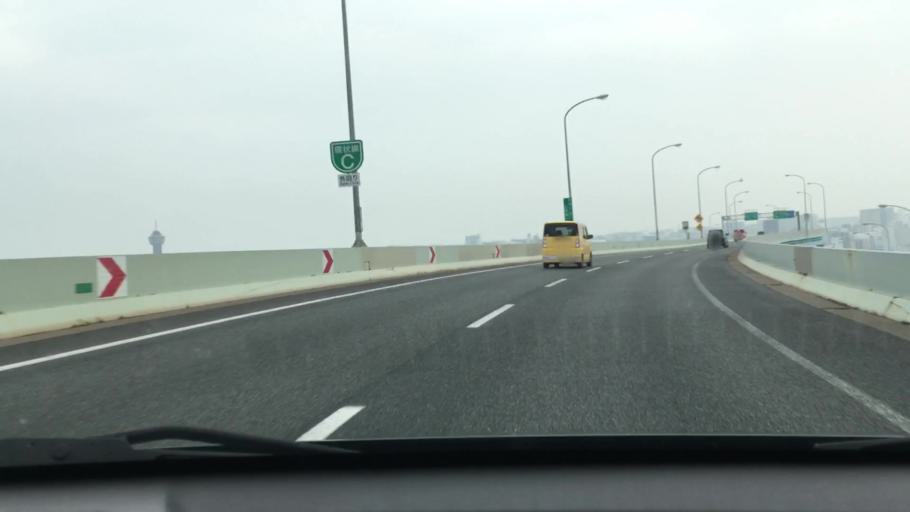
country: JP
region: Fukuoka
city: Fukuoka-shi
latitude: 33.6003
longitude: 130.3857
